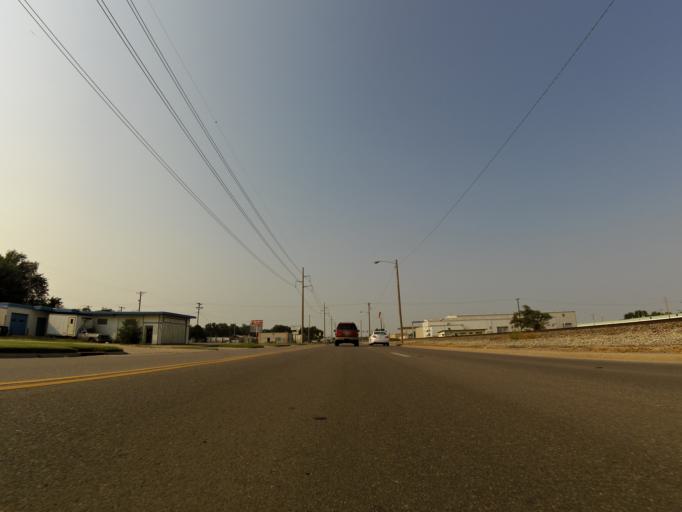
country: US
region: Kansas
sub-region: Sedgwick County
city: Wichita
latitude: 37.7437
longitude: -97.3360
